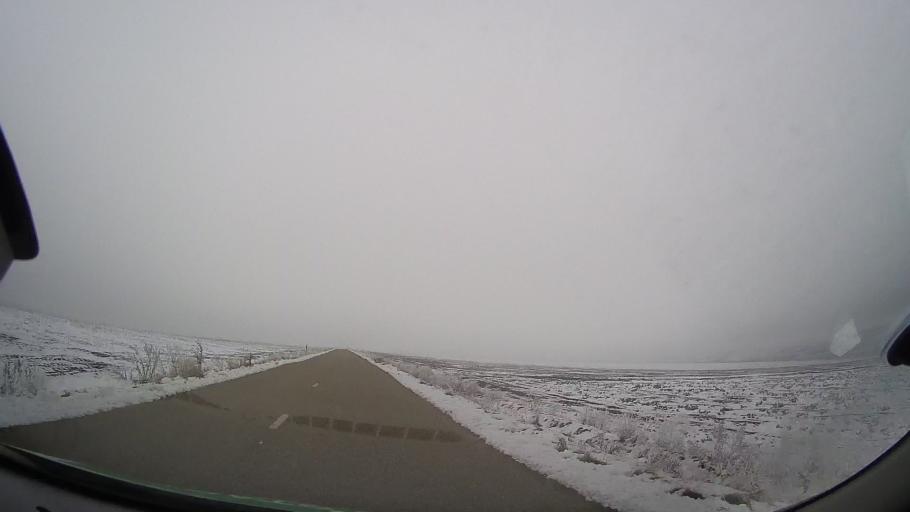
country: RO
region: Vaslui
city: Coroiesti
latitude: 46.2167
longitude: 27.4803
